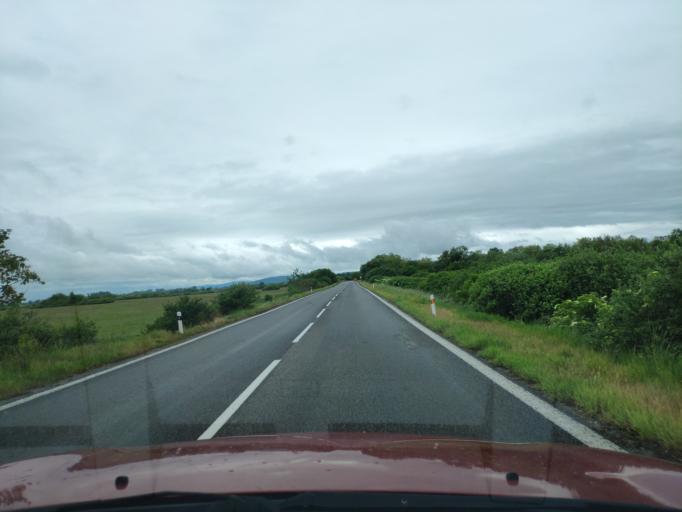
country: HU
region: Borsod-Abauj-Zemplen
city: Ricse
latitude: 48.4334
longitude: 21.8870
